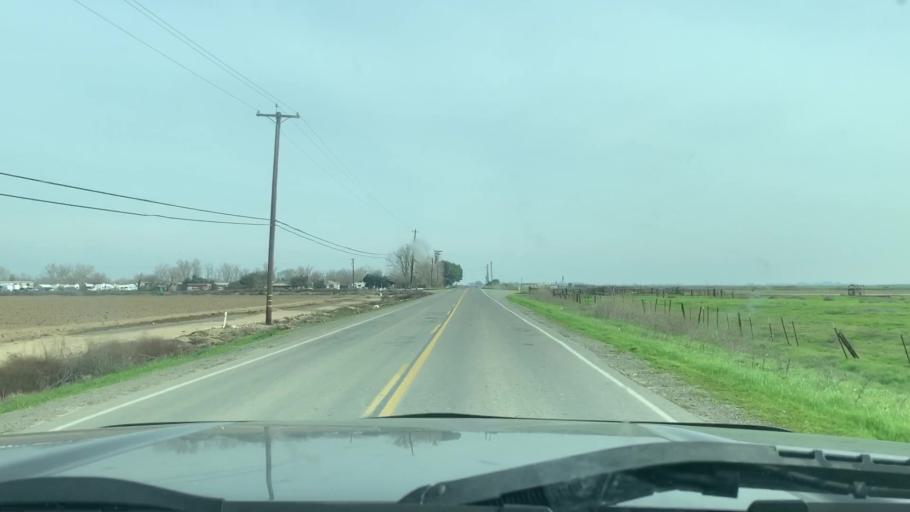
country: US
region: California
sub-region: Merced County
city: Los Banos
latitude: 37.0996
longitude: -120.8236
